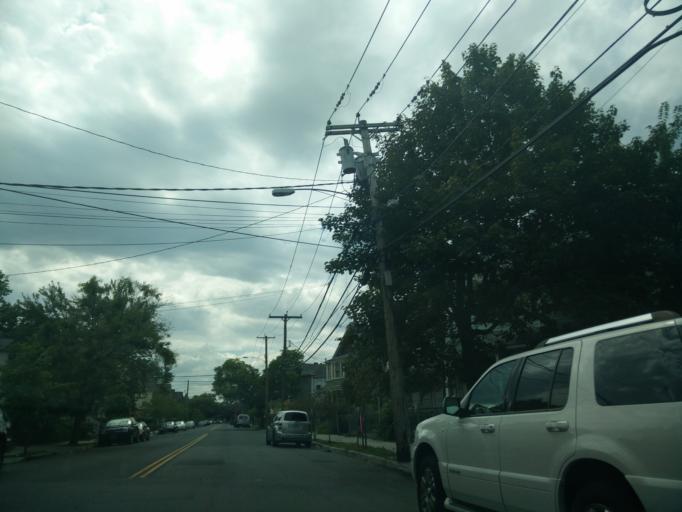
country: US
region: Connecticut
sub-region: Fairfield County
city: Bridgeport
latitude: 41.1725
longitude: -73.2012
